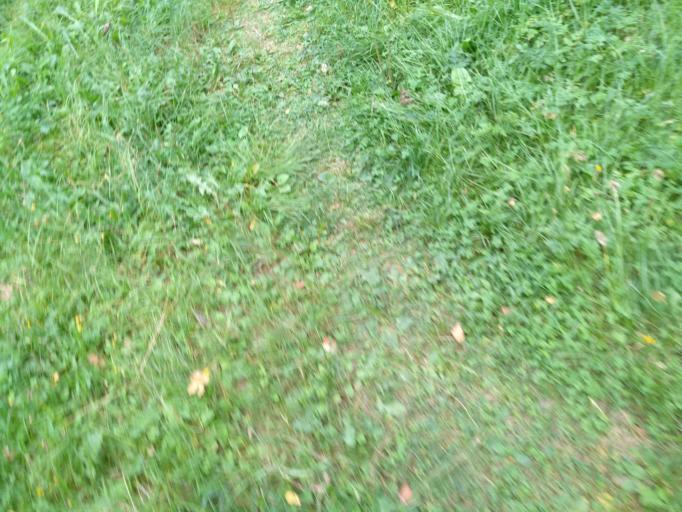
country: RU
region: Leningrad
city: Sapernoye
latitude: 60.6814
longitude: 29.9040
